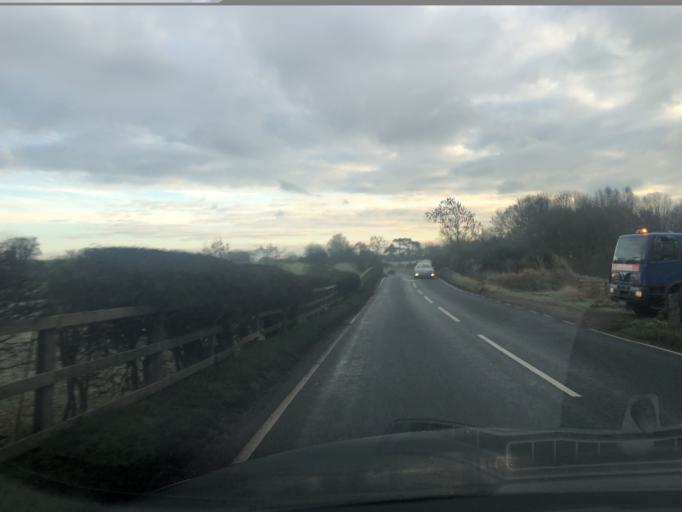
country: GB
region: England
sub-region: North Yorkshire
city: Northallerton
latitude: 54.3445
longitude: -1.4701
